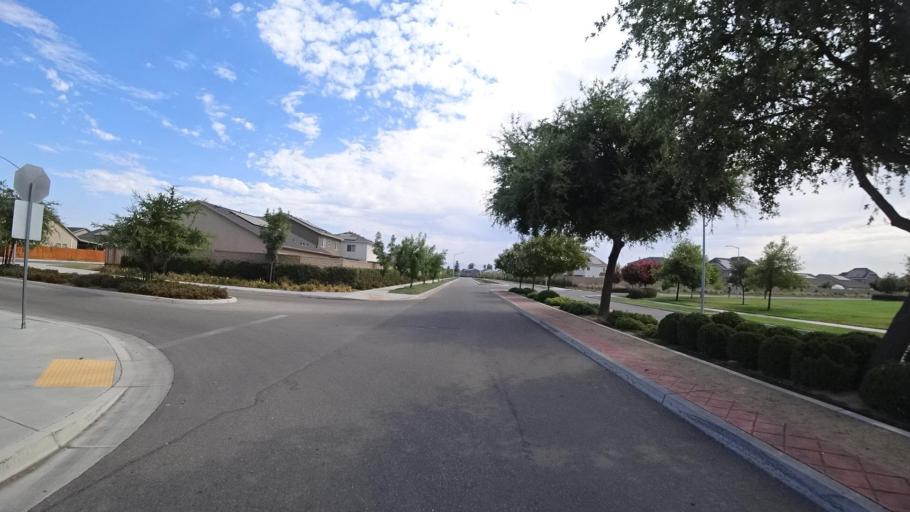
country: US
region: California
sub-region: Fresno County
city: Tarpey Village
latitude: 36.7838
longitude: -119.6684
